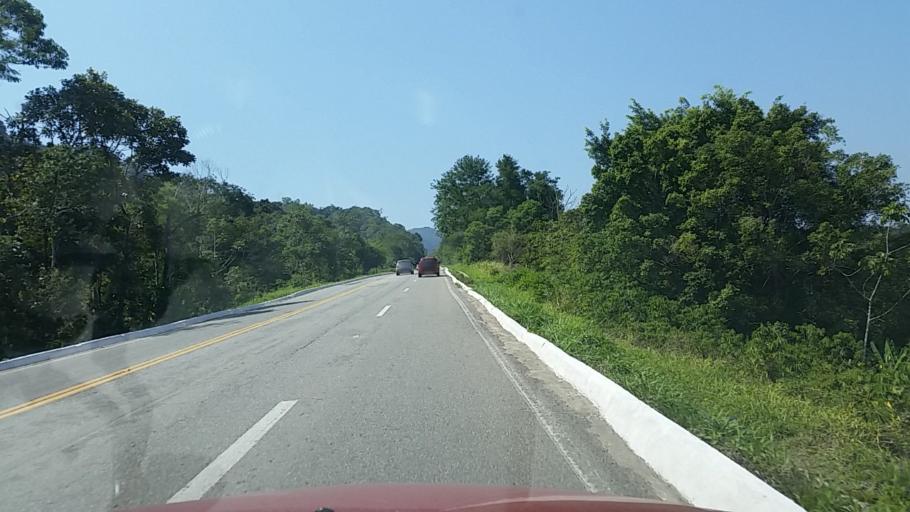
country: BR
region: Sao Paulo
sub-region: Miracatu
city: Miracatu
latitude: -24.3801
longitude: -47.5154
